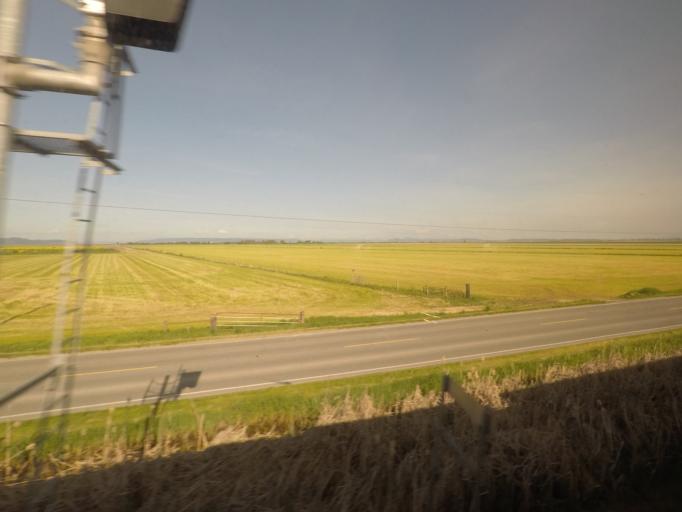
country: US
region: Washington
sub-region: Snohomish County
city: Stanwood
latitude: 48.2719
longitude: -122.3650
